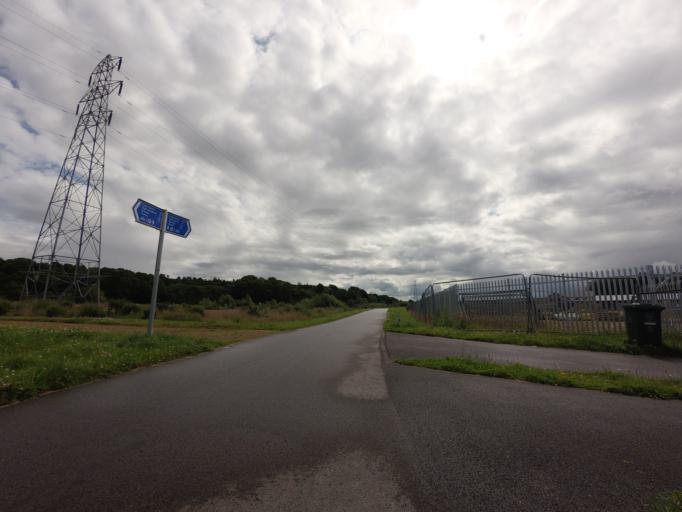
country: GB
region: Scotland
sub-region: Moray
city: Elgin
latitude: 57.6505
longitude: -3.2876
